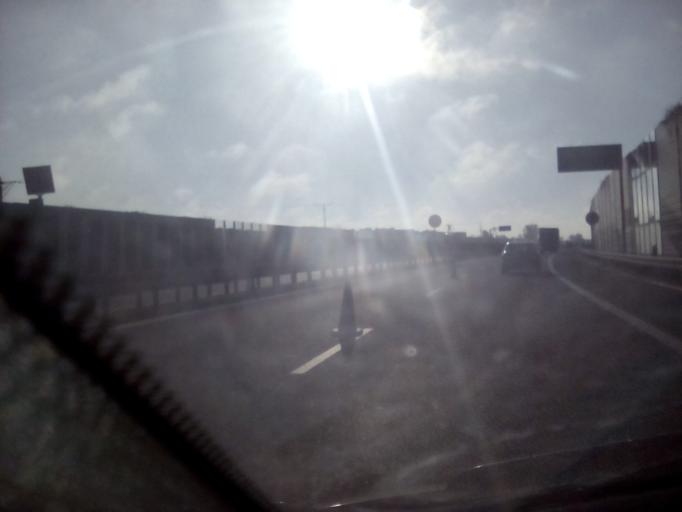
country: PL
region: Masovian Voivodeship
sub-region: Powiat grojecki
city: Grojec
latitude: 51.8547
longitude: 20.8657
